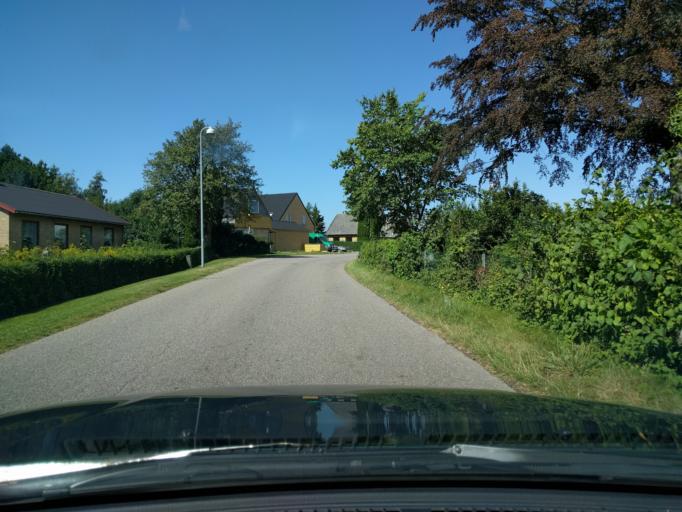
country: DK
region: Zealand
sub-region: Vordingborg Kommune
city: Neder Vindinge
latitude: 55.1126
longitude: 11.9001
